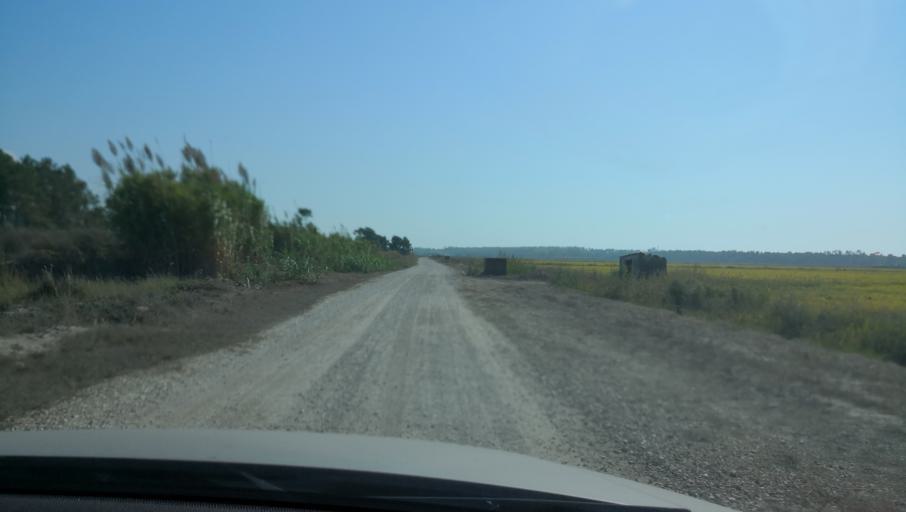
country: PT
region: Setubal
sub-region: Setubal
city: Setubal
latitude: 38.3965
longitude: -8.7881
